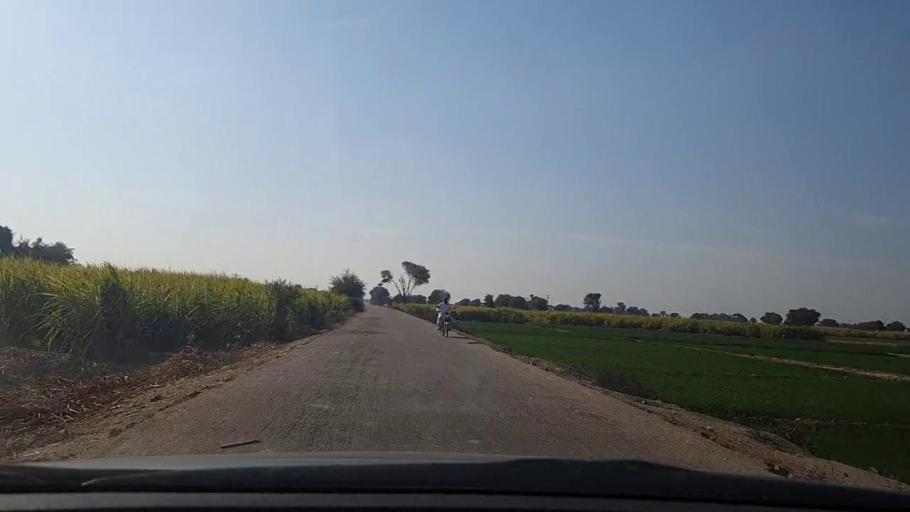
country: PK
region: Sindh
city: Daulatpur
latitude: 26.3211
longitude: 68.0252
